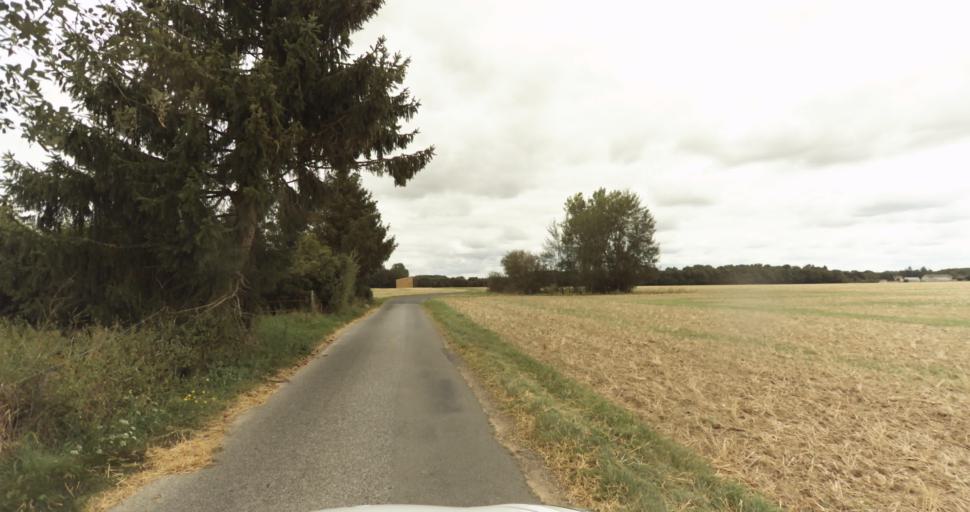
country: FR
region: Haute-Normandie
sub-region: Departement de l'Eure
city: La Madeleine-de-Nonancourt
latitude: 48.8358
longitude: 1.2023
